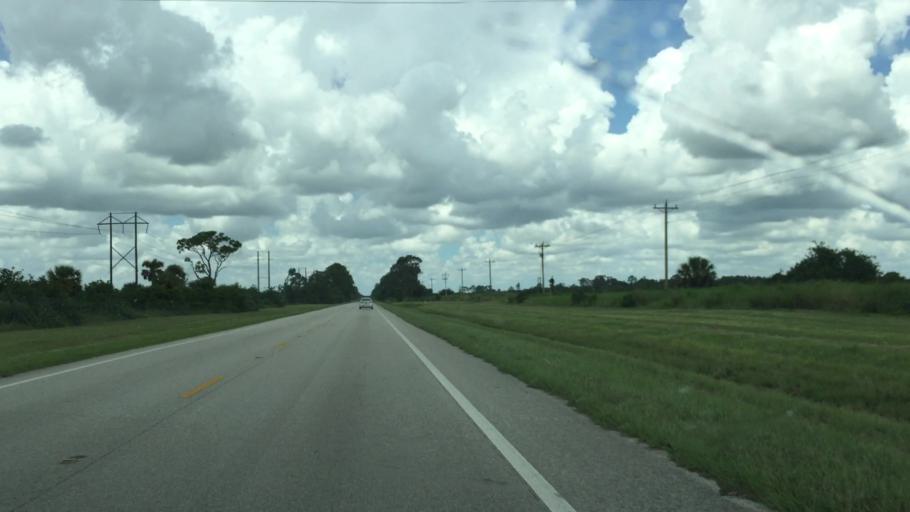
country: US
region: Florida
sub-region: Collier County
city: Immokalee
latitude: 26.5021
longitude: -81.5012
